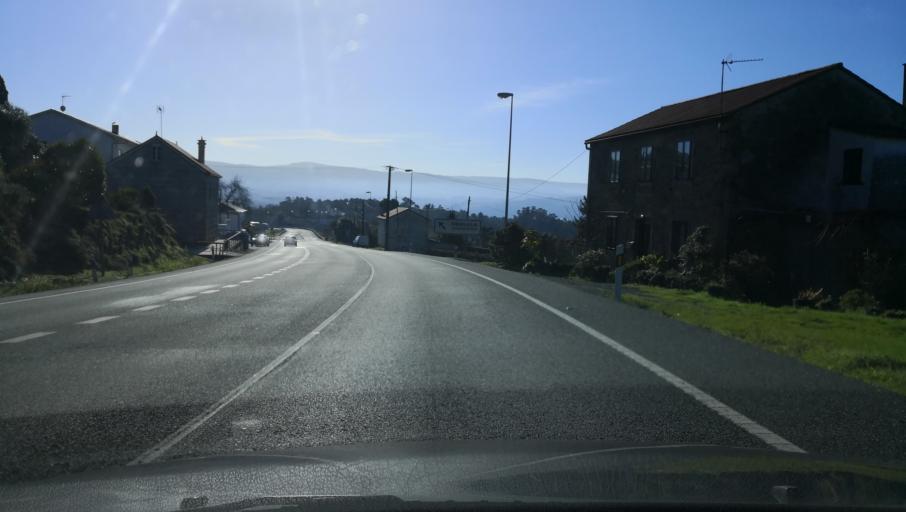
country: ES
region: Galicia
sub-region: Provincia da Coruna
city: Ribeira
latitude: 42.7790
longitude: -8.4280
